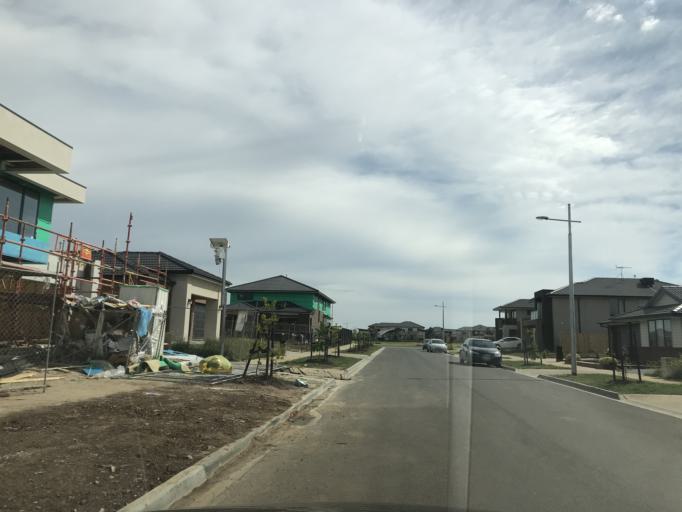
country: AU
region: Victoria
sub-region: Wyndham
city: Williams Landing
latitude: -37.8358
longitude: 144.7154
